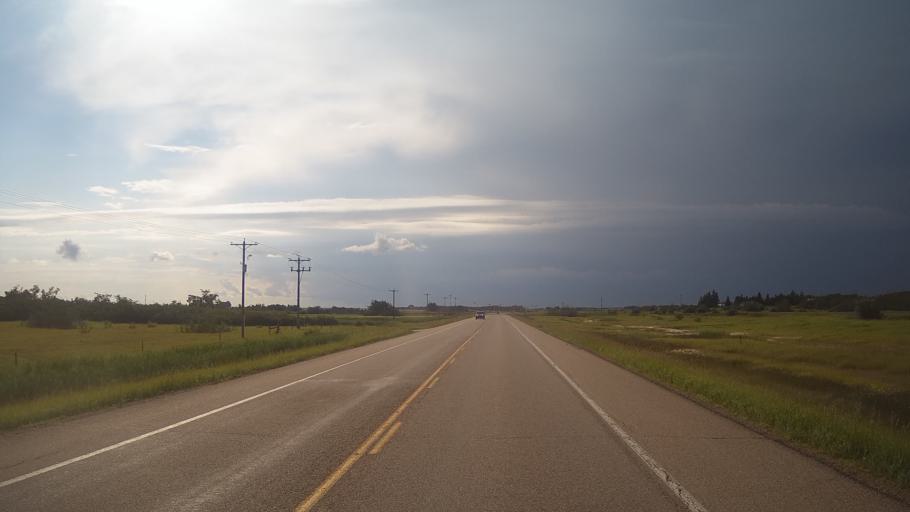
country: CA
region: Alberta
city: Viking
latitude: 53.1716
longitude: -112.0433
